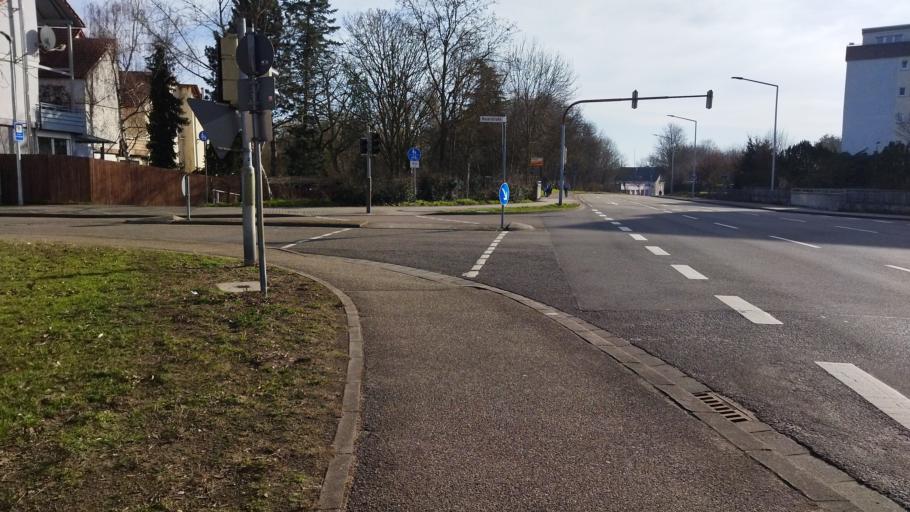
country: DE
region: Rheinland-Pfalz
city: Germersheim
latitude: 49.2084
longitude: 8.3644
